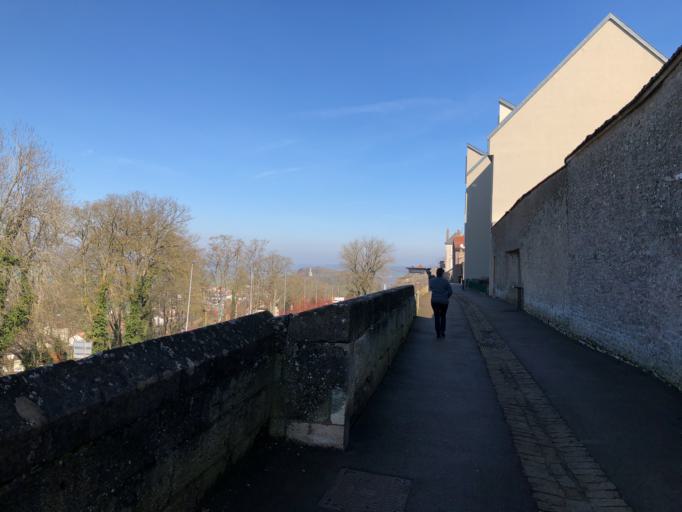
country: FR
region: Champagne-Ardenne
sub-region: Departement de la Haute-Marne
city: Langres
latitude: 47.8639
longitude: 5.3306
